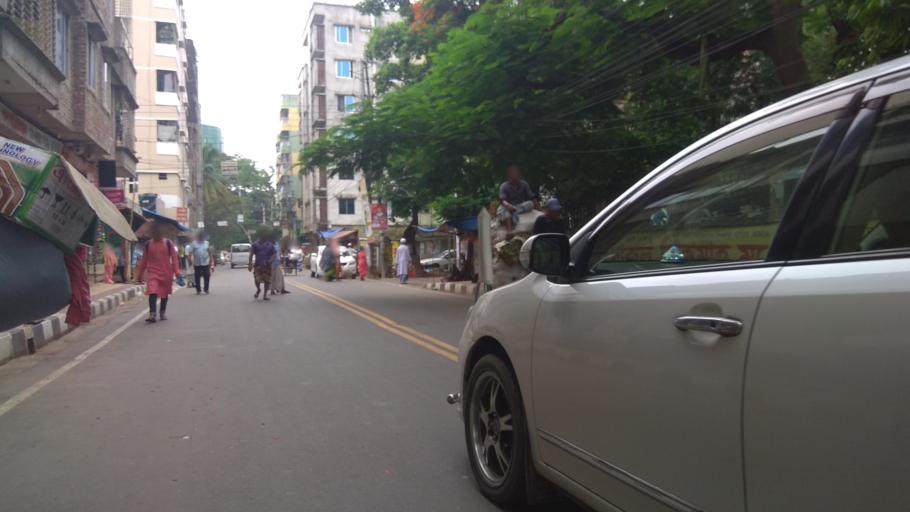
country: BD
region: Dhaka
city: Azimpur
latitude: 23.8062
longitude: 90.3607
